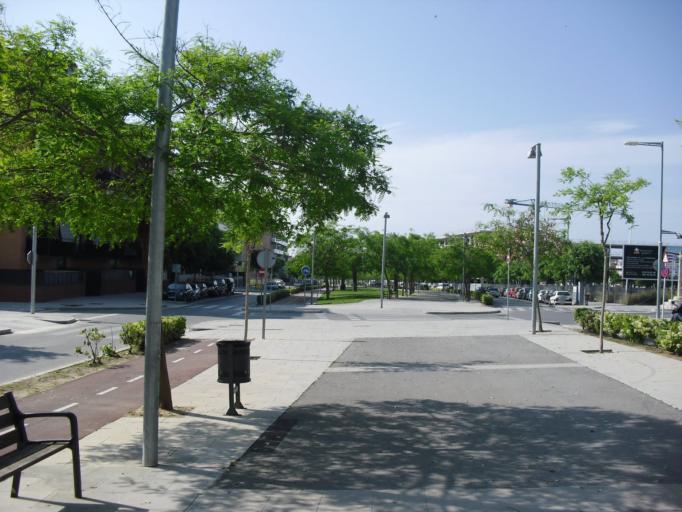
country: ES
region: Catalonia
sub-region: Provincia de Barcelona
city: Vilanova i la Geltru
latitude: 41.2301
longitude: 1.7297
